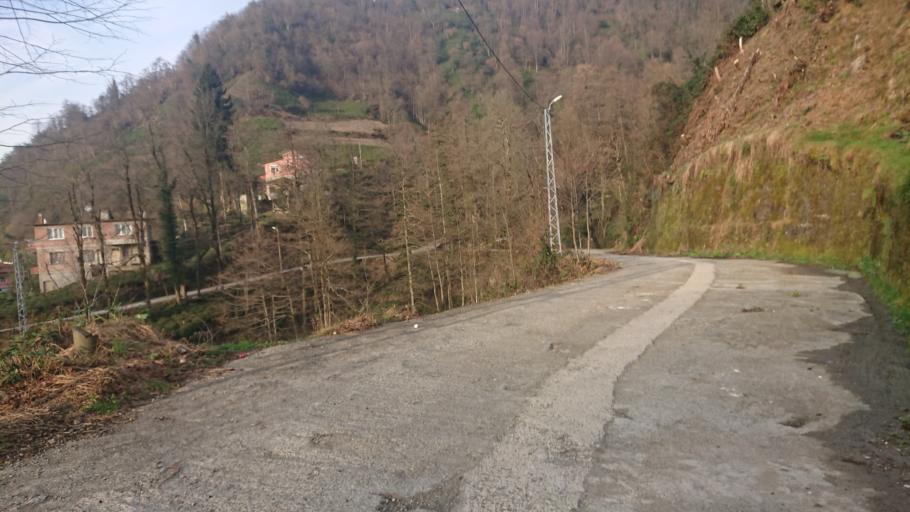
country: TR
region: Rize
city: Rize
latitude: 40.9800
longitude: 40.4961
